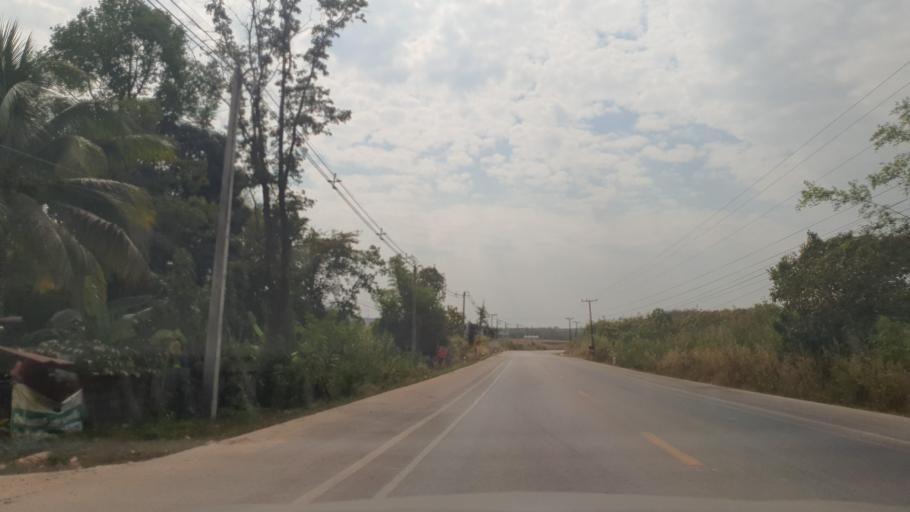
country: TH
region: Changwat Bueng Kan
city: Si Wilai
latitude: 18.2931
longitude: 103.7999
